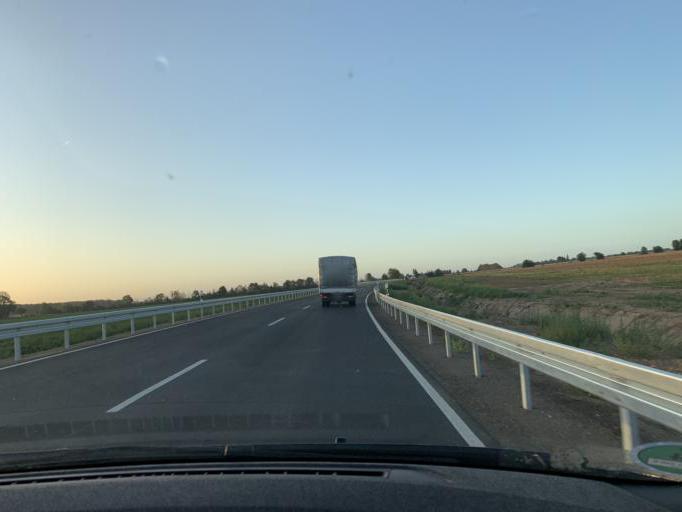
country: DE
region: North Rhine-Westphalia
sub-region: Regierungsbezirk Koln
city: Vettweiss
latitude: 50.7284
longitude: 6.5717
